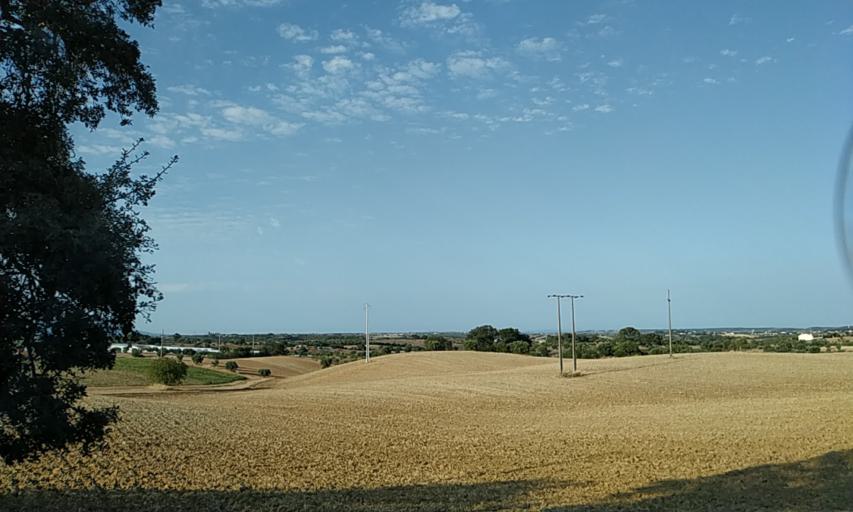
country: PT
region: Santarem
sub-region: Alcanena
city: Alcanena
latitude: 39.3481
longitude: -8.6640
